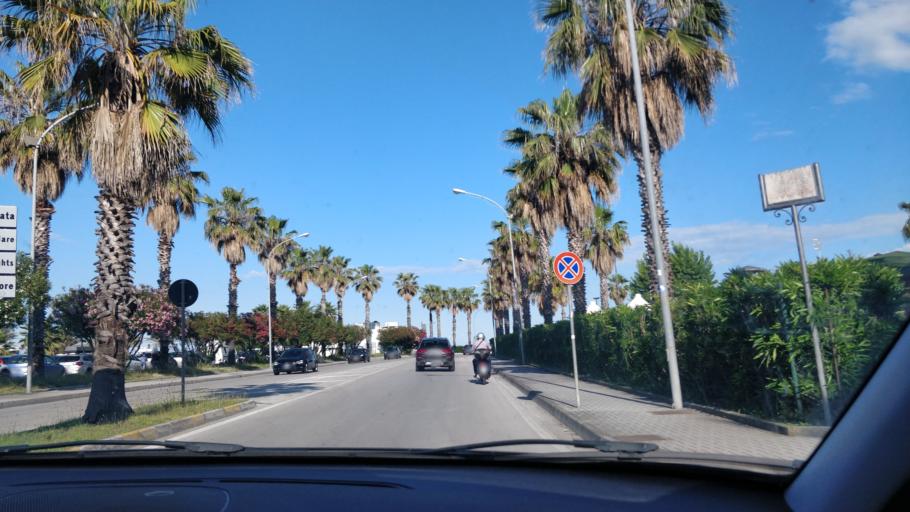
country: IT
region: The Marches
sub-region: Provincia di Ascoli Piceno
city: Grottammare
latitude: 42.9522
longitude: 13.8872
